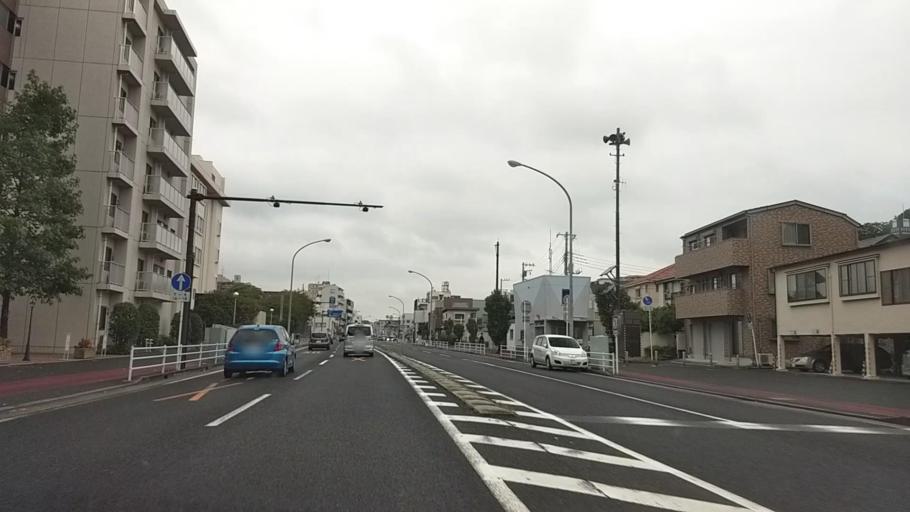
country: JP
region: Kanagawa
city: Yokohama
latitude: 35.4183
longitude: 139.6424
